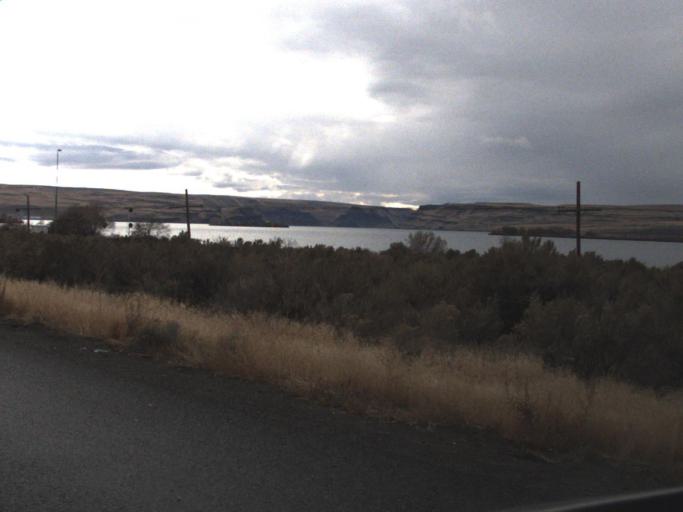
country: US
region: Washington
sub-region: Benton County
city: Finley
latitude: 46.1194
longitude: -118.9271
